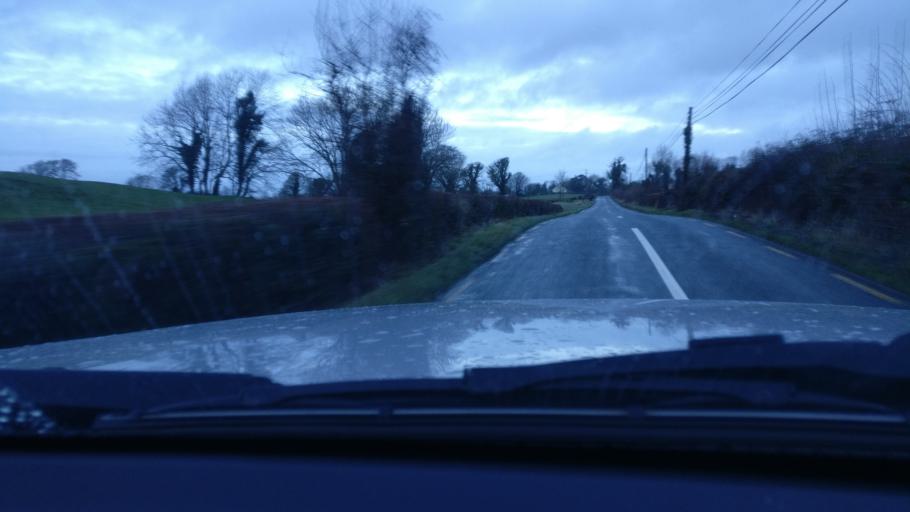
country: IE
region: Connaught
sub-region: County Galway
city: Ballinasloe
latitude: 53.2597
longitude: -8.2563
